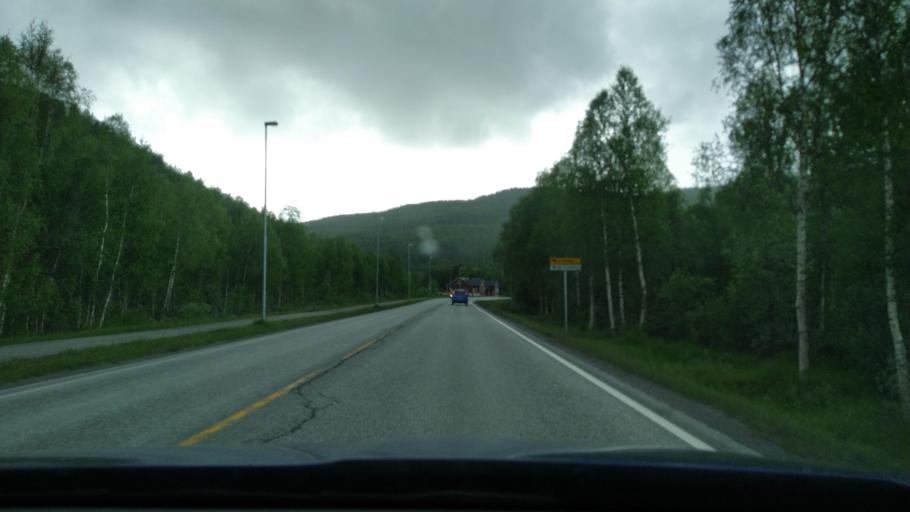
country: NO
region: Troms
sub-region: Malselv
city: Moen
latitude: 69.0090
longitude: 18.5006
